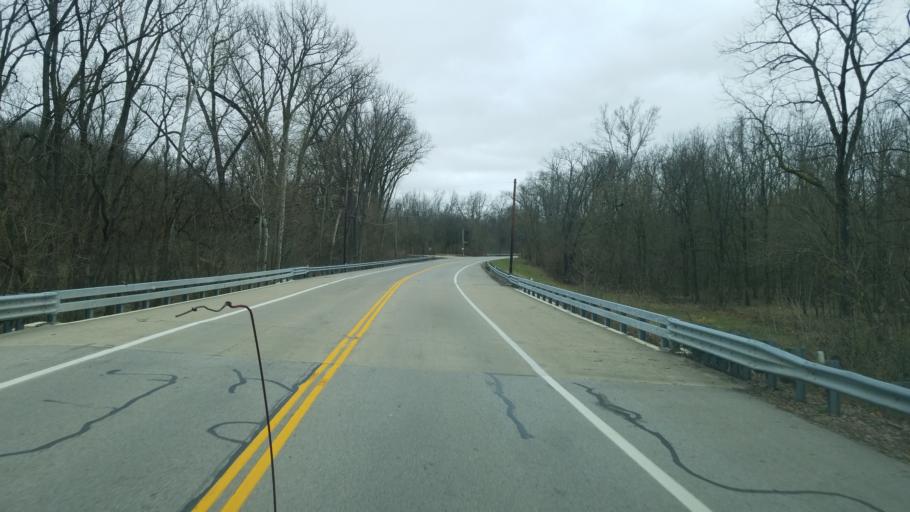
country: US
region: Ohio
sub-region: Clermont County
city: New Richmond
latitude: 38.8221
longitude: -84.2162
